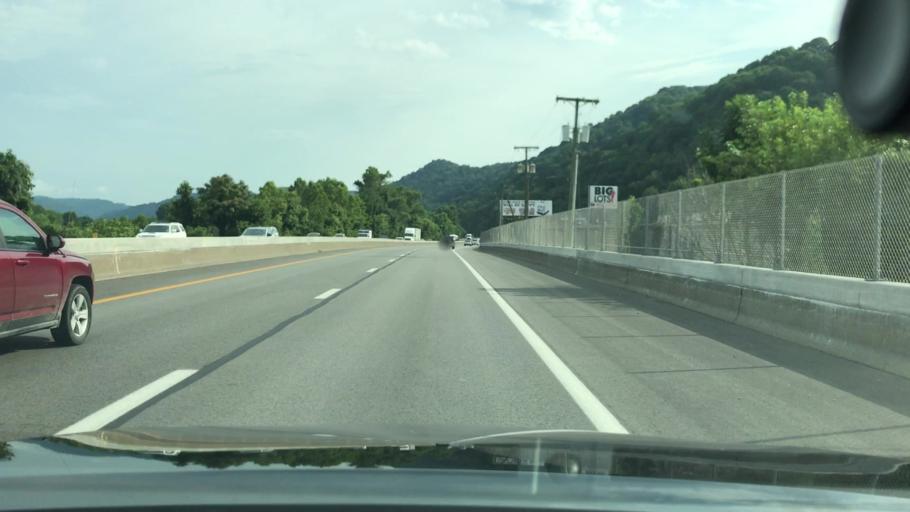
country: US
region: West Virginia
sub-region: Kanawha County
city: Rand
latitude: 38.2932
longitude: -81.5660
